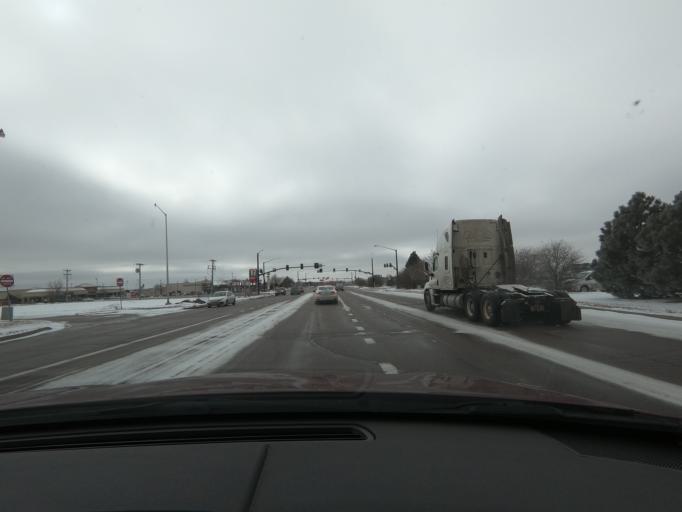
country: US
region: Colorado
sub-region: El Paso County
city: Security-Widefield
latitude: 38.7215
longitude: -104.7002
